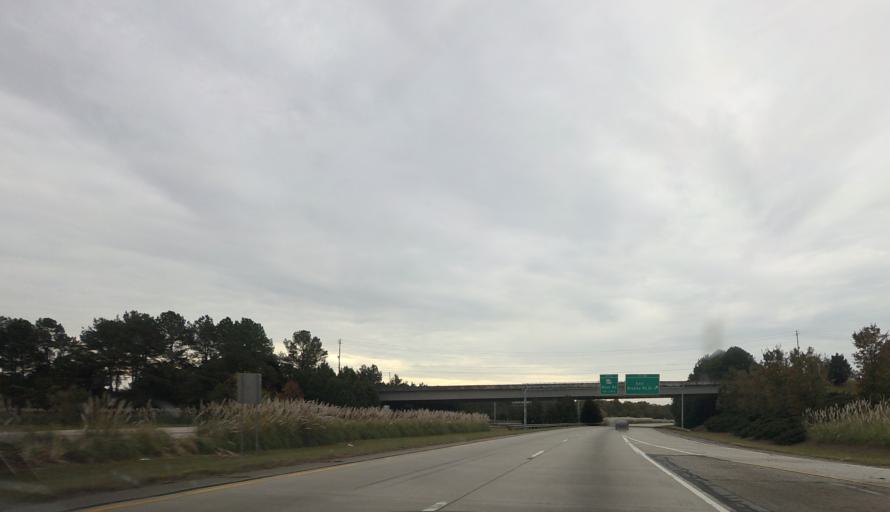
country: US
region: Alabama
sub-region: Russell County
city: Phenix City
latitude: 32.5328
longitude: -84.9745
